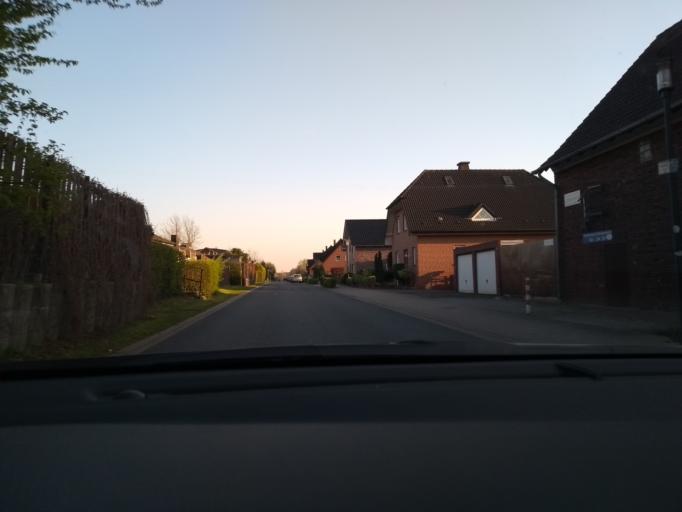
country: DE
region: North Rhine-Westphalia
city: Selm
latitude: 51.6929
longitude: 7.4554
